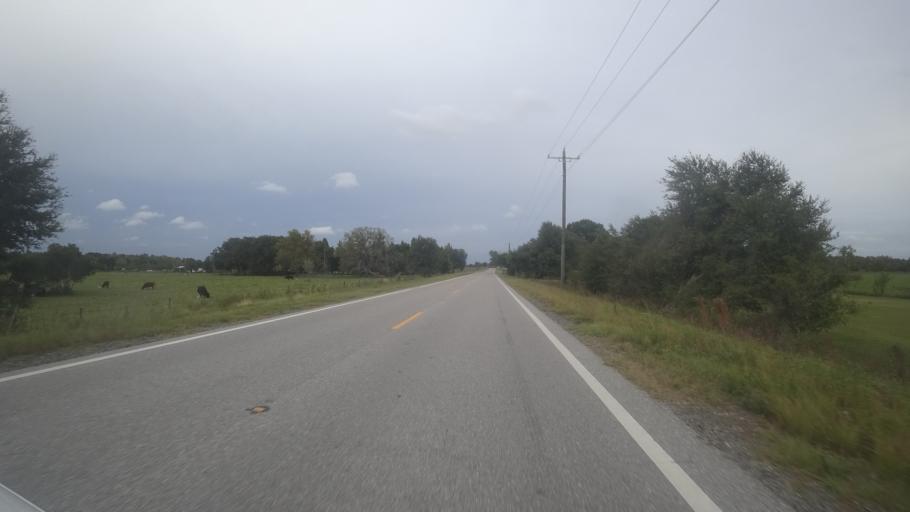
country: US
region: Florida
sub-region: Sarasota County
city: The Meadows
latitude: 27.4689
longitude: -82.2704
